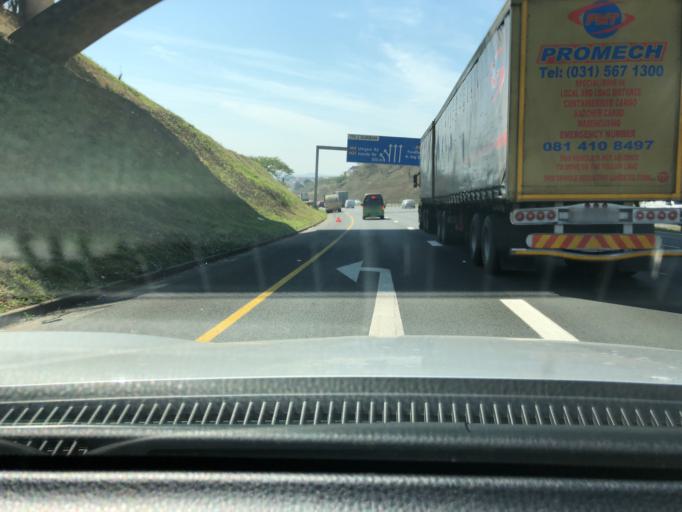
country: ZA
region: KwaZulu-Natal
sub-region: eThekwini Metropolitan Municipality
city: Berea
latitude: -29.8177
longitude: 30.9711
